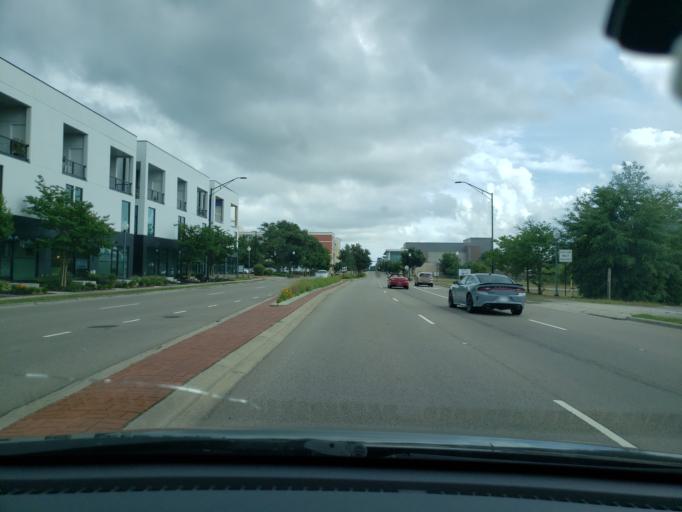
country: US
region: North Carolina
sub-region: New Hanover County
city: Wilmington
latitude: 34.2476
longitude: -77.9475
